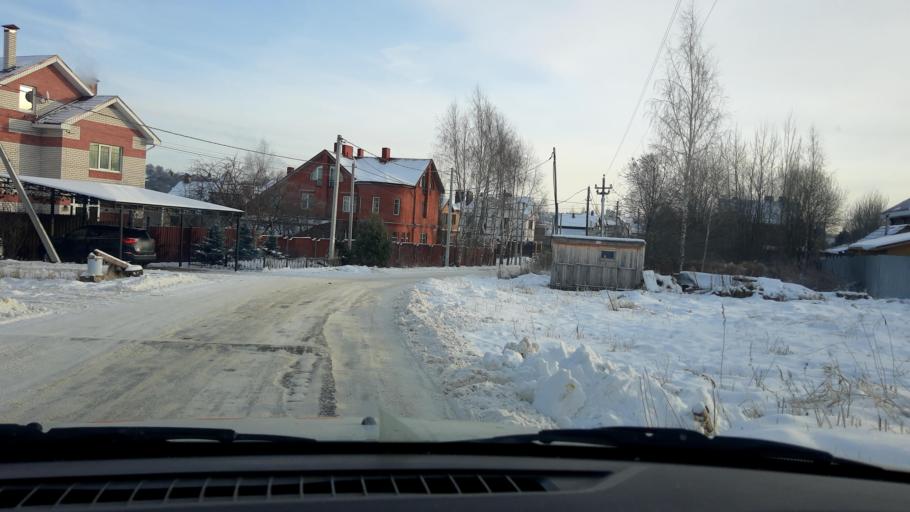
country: RU
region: Nizjnij Novgorod
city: Afonino
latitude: 56.2699
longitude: 44.0663
